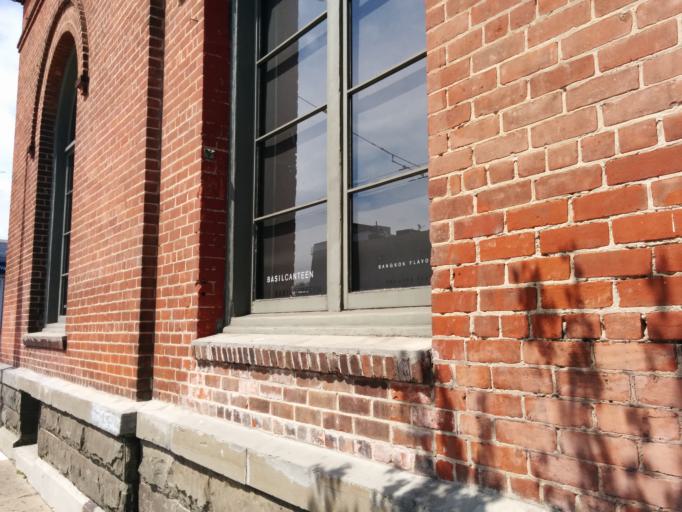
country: US
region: California
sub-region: San Francisco County
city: San Francisco
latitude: 37.7716
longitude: -122.4137
